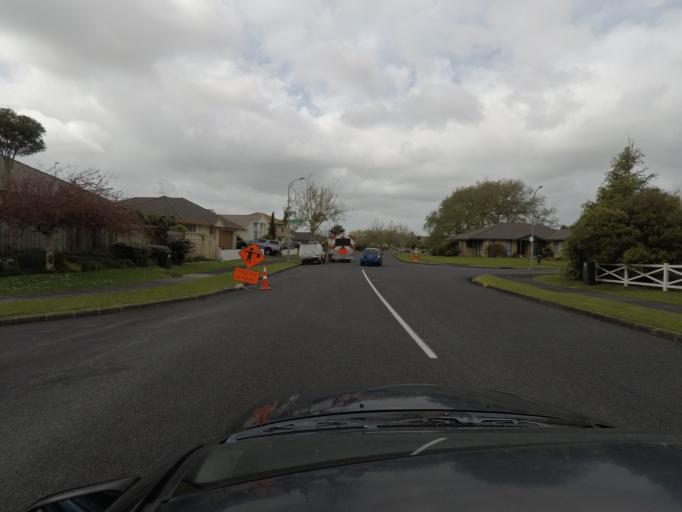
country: NZ
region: Auckland
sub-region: Auckland
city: Pakuranga
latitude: -36.9248
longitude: 174.9177
